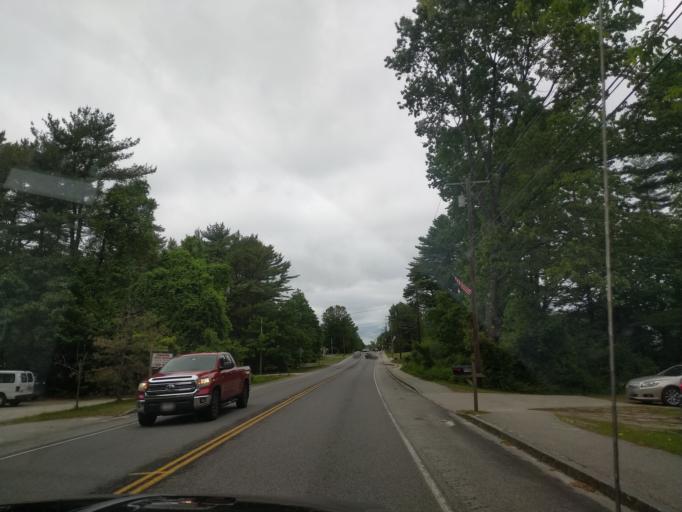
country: US
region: Maine
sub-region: Cumberland County
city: North Windham
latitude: 43.8368
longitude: -70.4267
